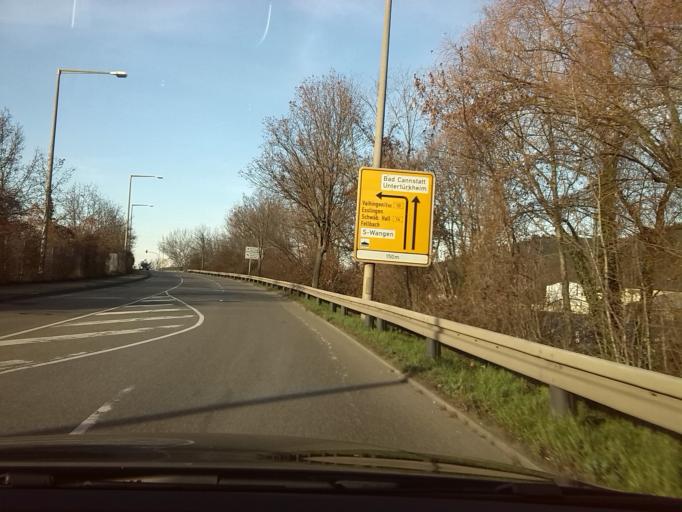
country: DE
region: Baden-Wuerttemberg
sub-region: Regierungsbezirk Stuttgart
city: Fellbach
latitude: 48.7704
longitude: 9.2605
